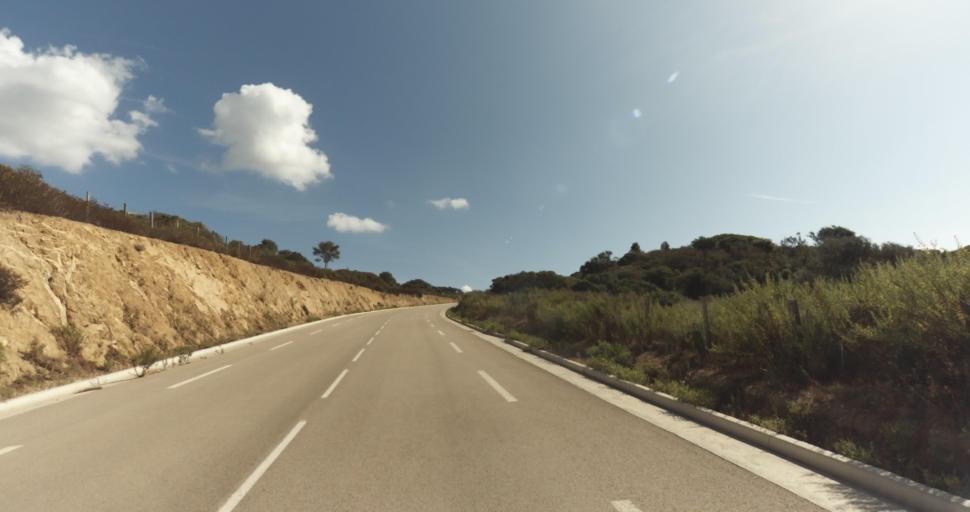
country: FR
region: Corsica
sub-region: Departement de la Corse-du-Sud
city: Ajaccio
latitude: 41.9326
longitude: 8.6762
